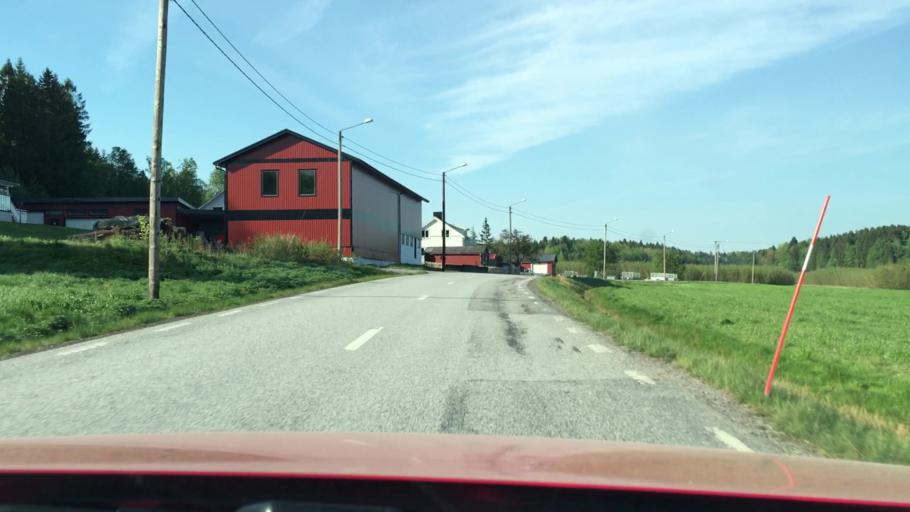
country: SE
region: Vaestra Goetaland
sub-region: Munkedals Kommun
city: Munkedal
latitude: 58.6011
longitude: 11.5562
